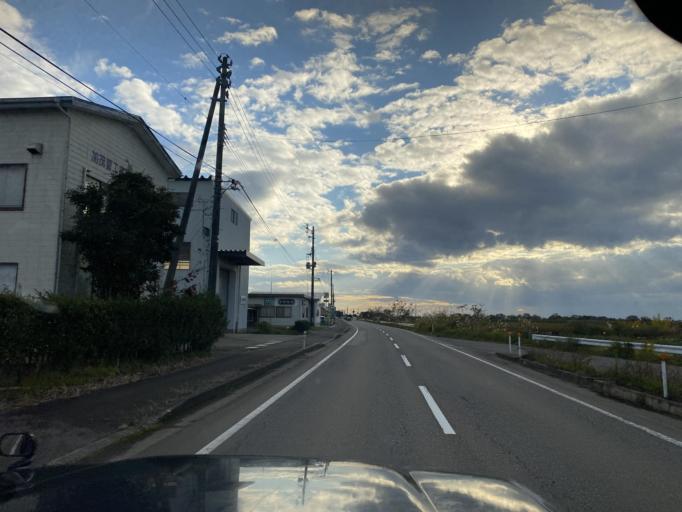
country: JP
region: Niigata
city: Kamo
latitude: 37.6772
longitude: 139.0157
